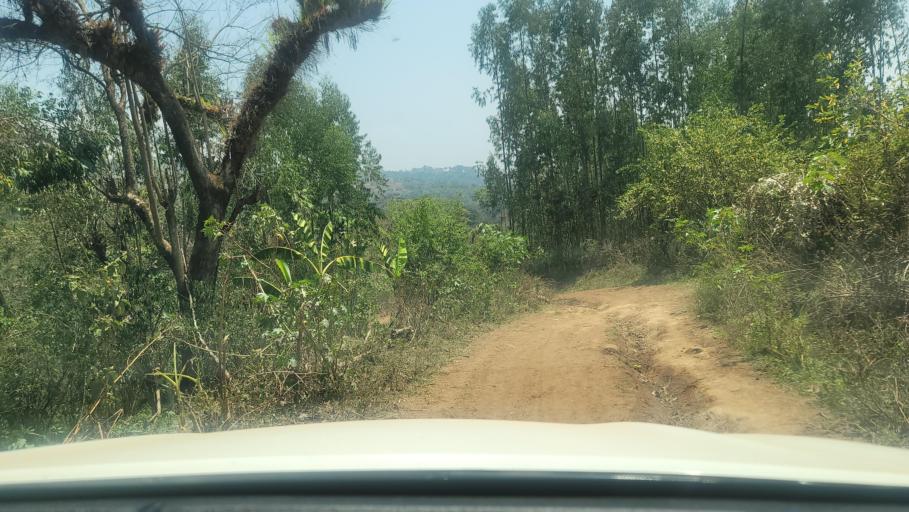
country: ET
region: Southern Nations, Nationalities, and People's Region
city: Bonga
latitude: 7.5285
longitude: 36.1947
